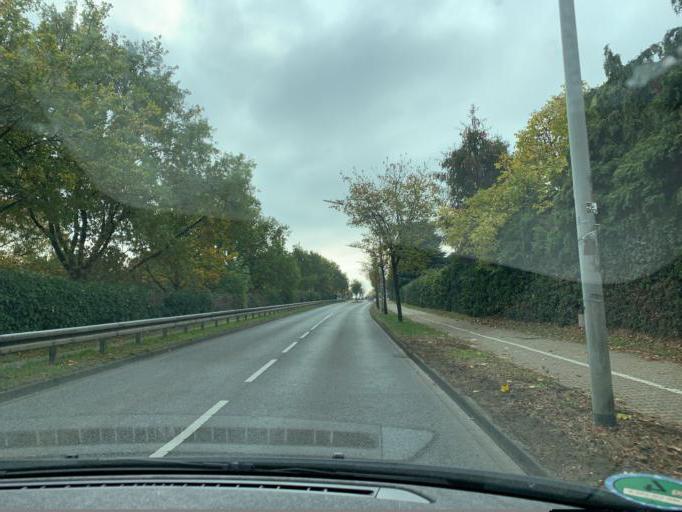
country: DE
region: North Rhine-Westphalia
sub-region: Regierungsbezirk Dusseldorf
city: Monchengladbach
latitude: 51.1553
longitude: 6.4408
